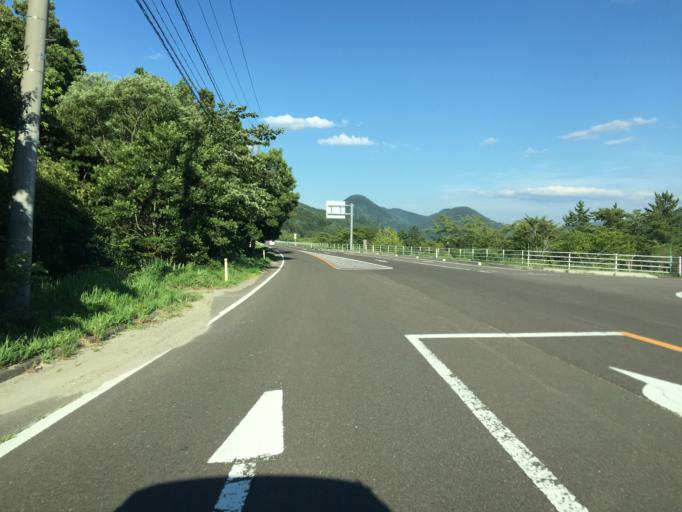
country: JP
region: Miyagi
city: Shiroishi
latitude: 37.9829
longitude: 140.4688
